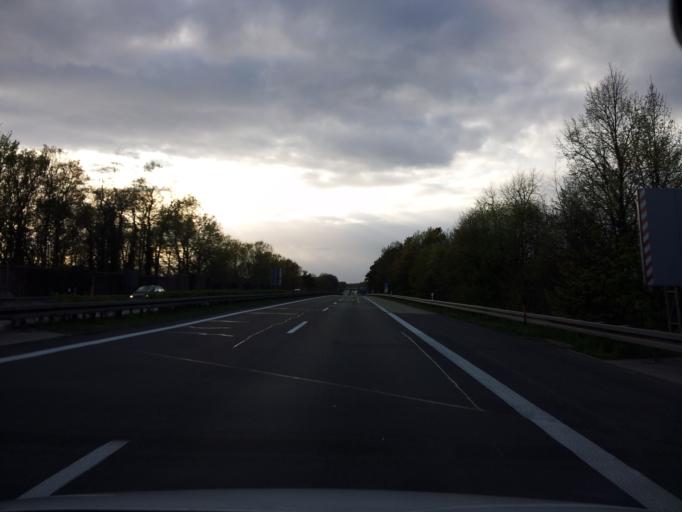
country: DE
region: Brandenburg
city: Lubbenau
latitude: 51.8298
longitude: 13.9899
